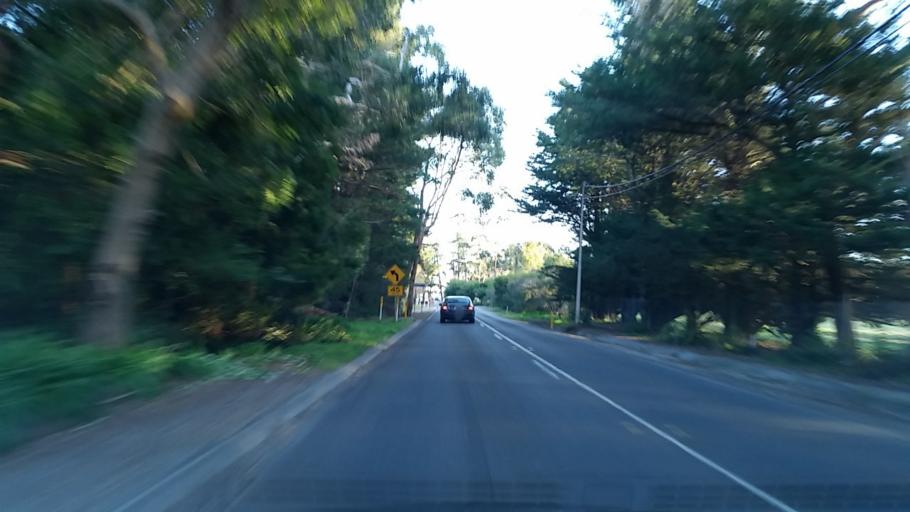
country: AU
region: South Australia
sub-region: Adelaide Hills
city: Upper Sturt
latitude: -35.0561
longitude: 138.6798
